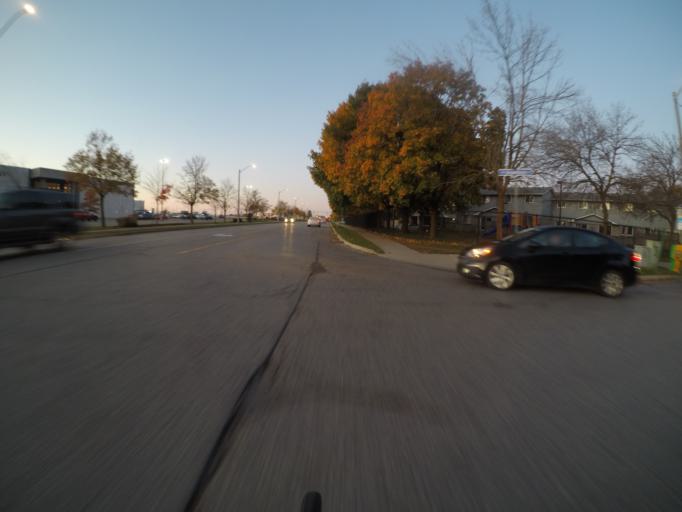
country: CA
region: Ontario
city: Kitchener
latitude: 43.4245
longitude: -80.4412
